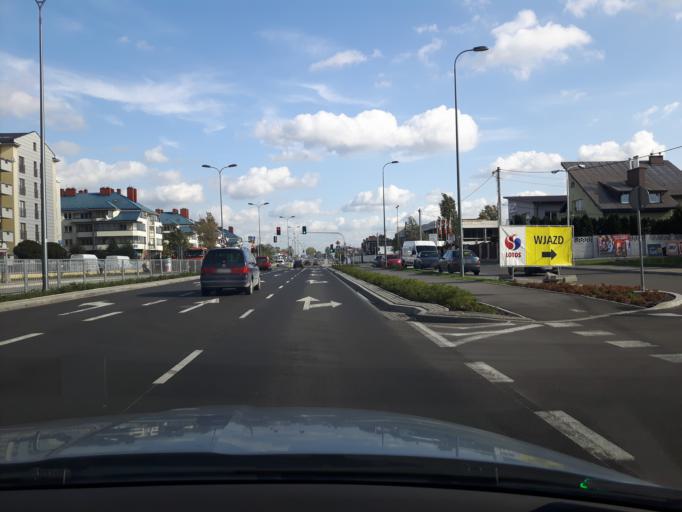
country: PL
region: Masovian Voivodeship
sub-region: Powiat wolominski
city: Zabki
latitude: 52.2866
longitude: 21.0814
